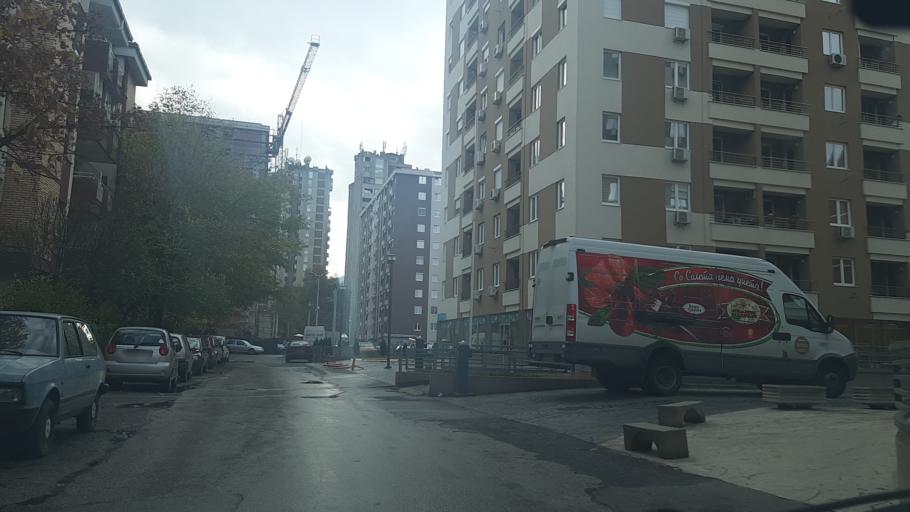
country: MK
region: Karpos
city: Skopje
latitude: 41.9875
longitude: 21.4555
